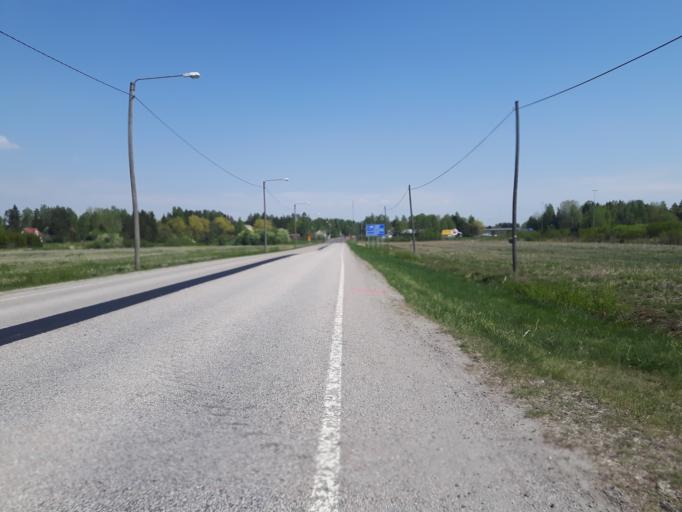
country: FI
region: Uusimaa
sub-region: Helsinki
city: Nickby
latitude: 60.3090
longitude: 25.3823
